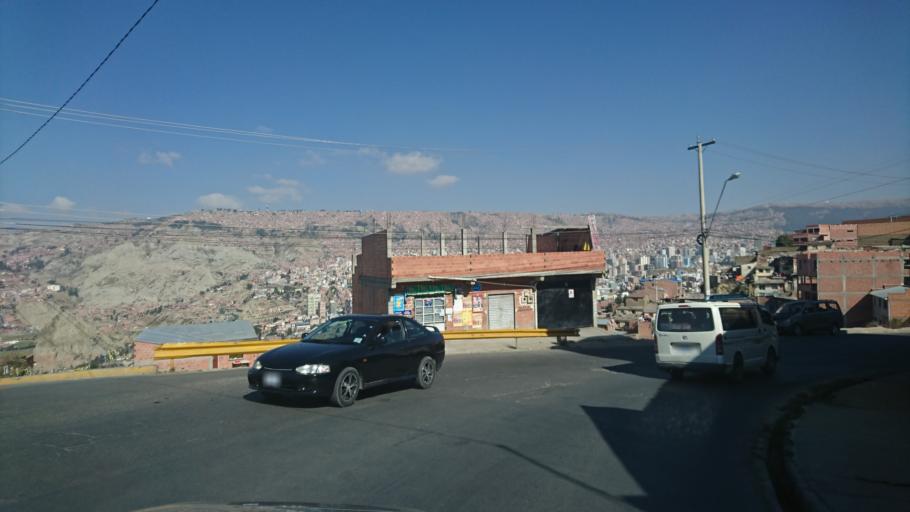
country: BO
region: La Paz
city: La Paz
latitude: -16.5107
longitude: -68.1057
